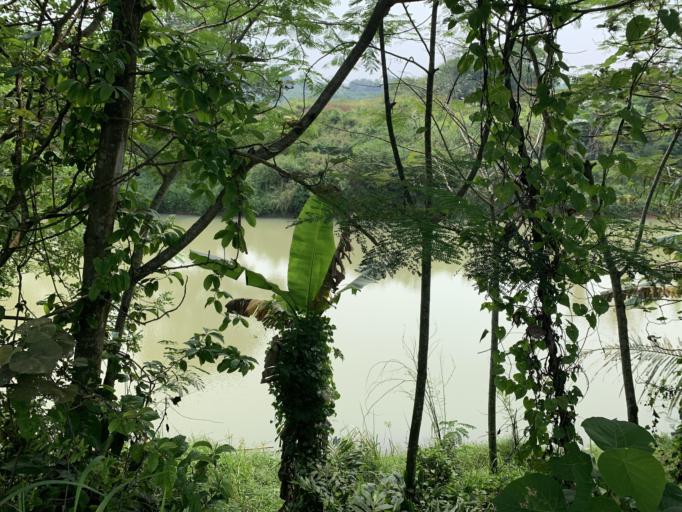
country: ID
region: West Java
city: Serpong
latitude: -6.3880
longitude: 106.5775
